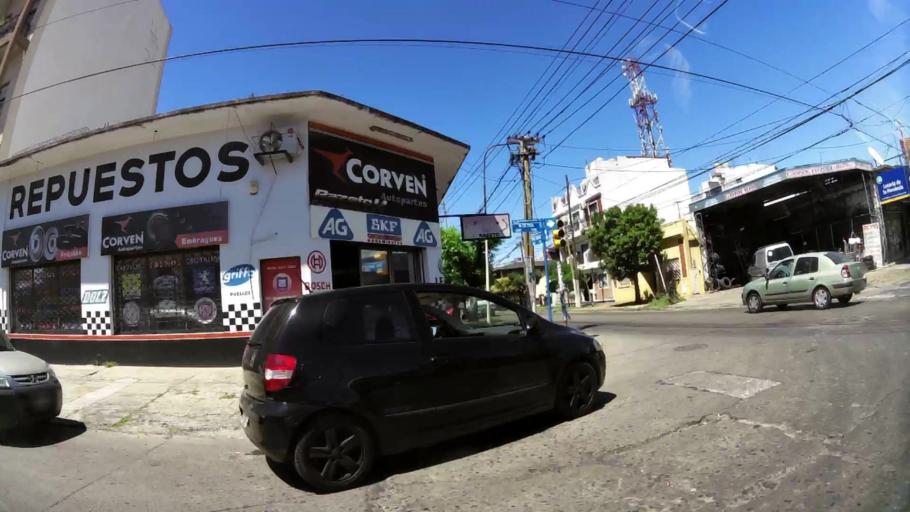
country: AR
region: Buenos Aires
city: Caseros
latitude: -34.6010
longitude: -58.5690
